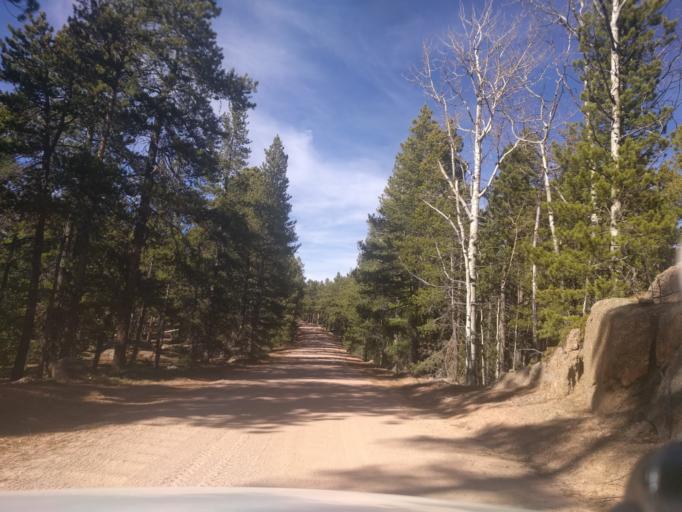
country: US
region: Colorado
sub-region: Douglas County
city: Perry Park
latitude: 39.2072
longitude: -105.0546
